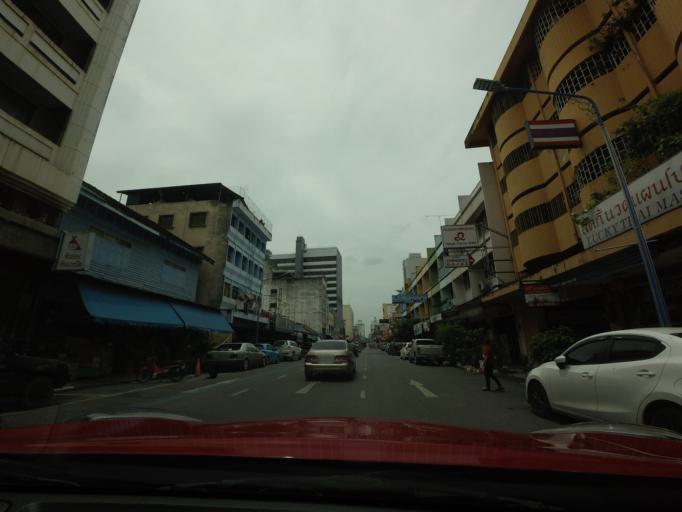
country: TH
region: Songkhla
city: Hat Yai
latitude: 6.9983
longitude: 100.4710
